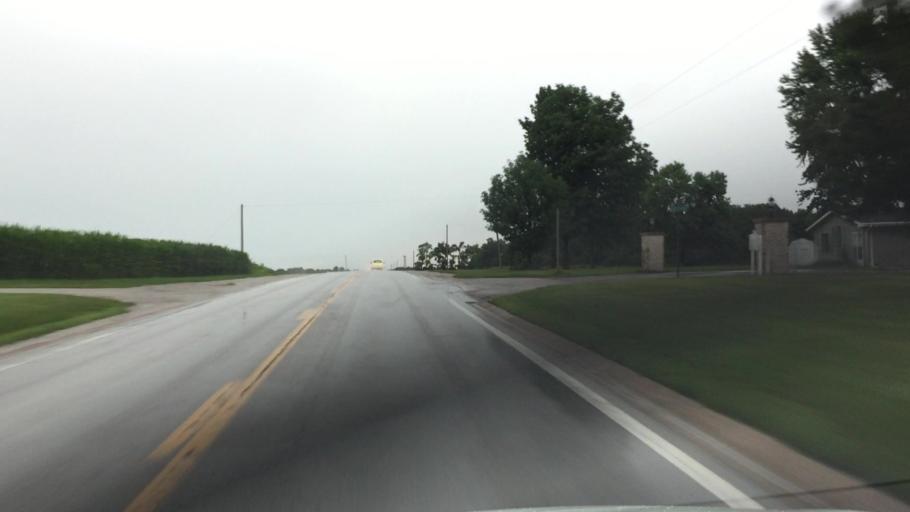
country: US
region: Illinois
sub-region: Hancock County
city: Carthage
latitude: 40.4418
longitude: -91.1399
